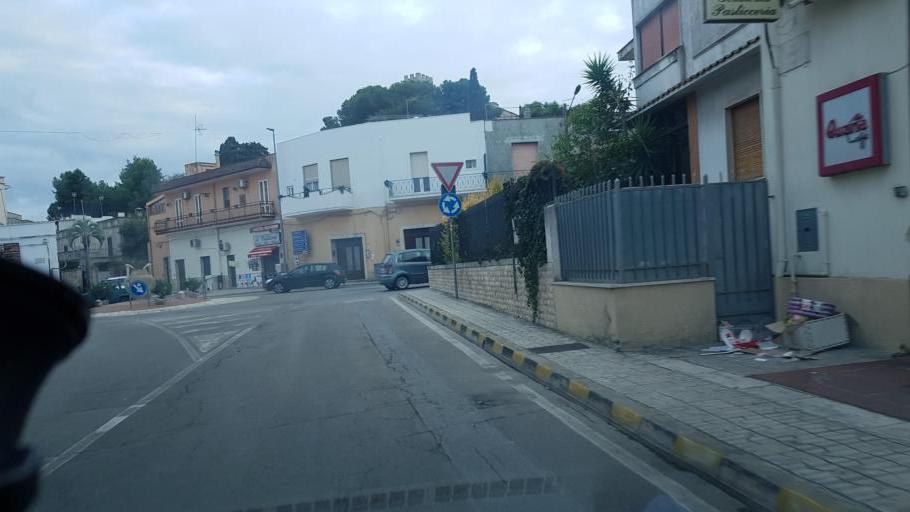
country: IT
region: Apulia
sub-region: Provincia di Brindisi
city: Oria
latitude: 40.5020
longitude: 17.6409
